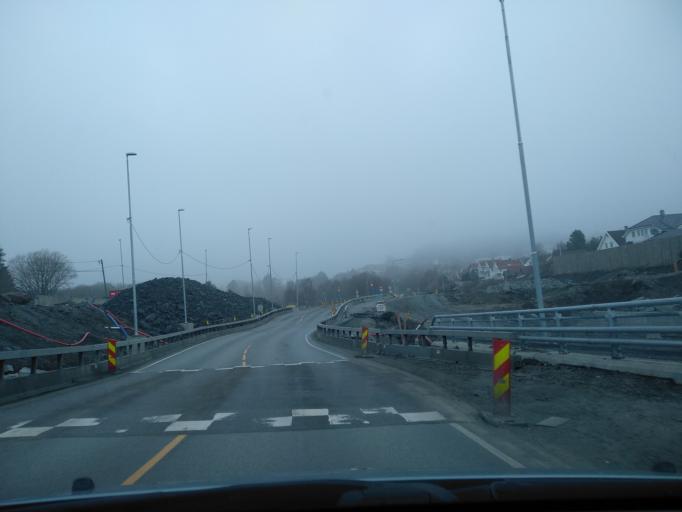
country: NO
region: Rogaland
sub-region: Stavanger
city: Stavanger
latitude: 58.9792
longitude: 5.6847
